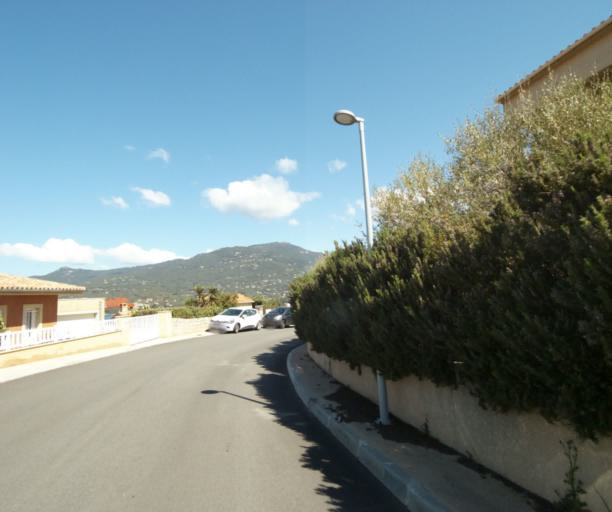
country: FR
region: Corsica
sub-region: Departement de la Corse-du-Sud
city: Propriano
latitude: 41.6761
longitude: 8.9107
